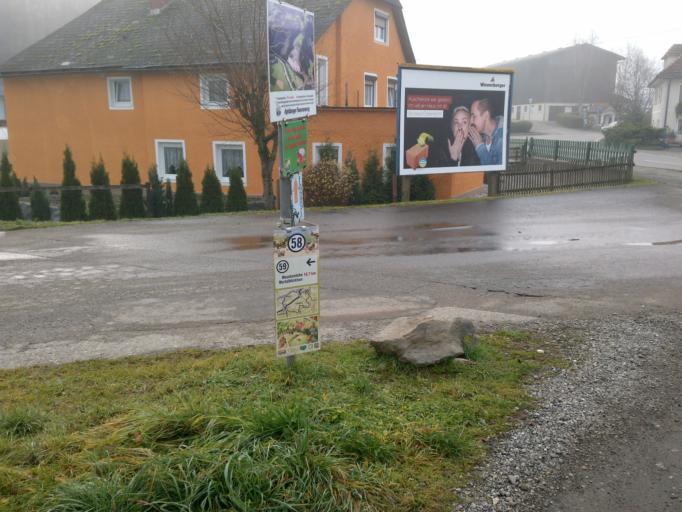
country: AT
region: Styria
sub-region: Politischer Bezirk Murtal
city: Apfelberg
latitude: 47.1987
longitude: 14.8370
